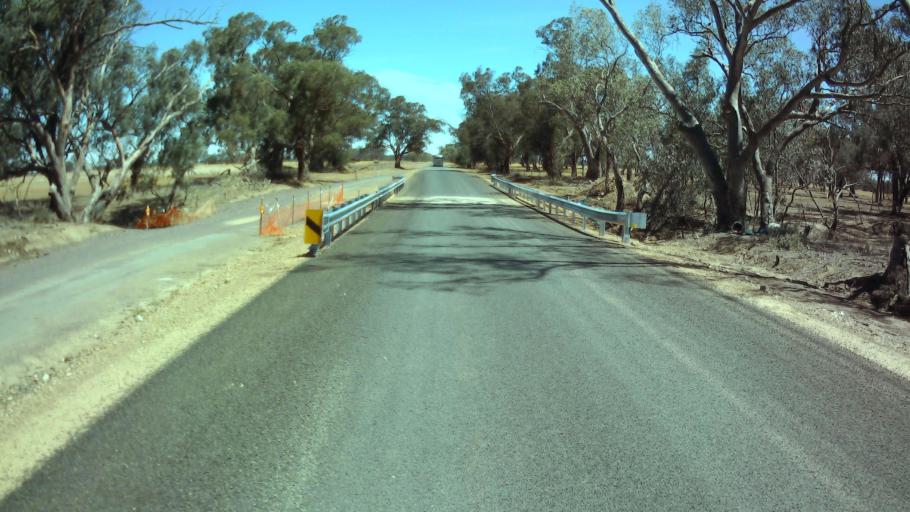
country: AU
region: New South Wales
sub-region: Weddin
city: Grenfell
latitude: -33.8430
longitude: 147.6970
